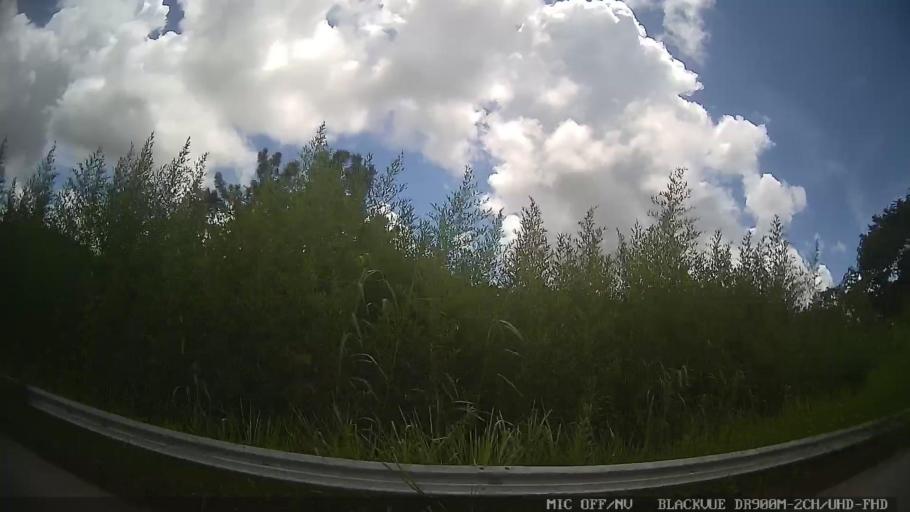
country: BR
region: Sao Paulo
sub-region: Amparo
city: Amparo
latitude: -22.7673
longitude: -46.7441
